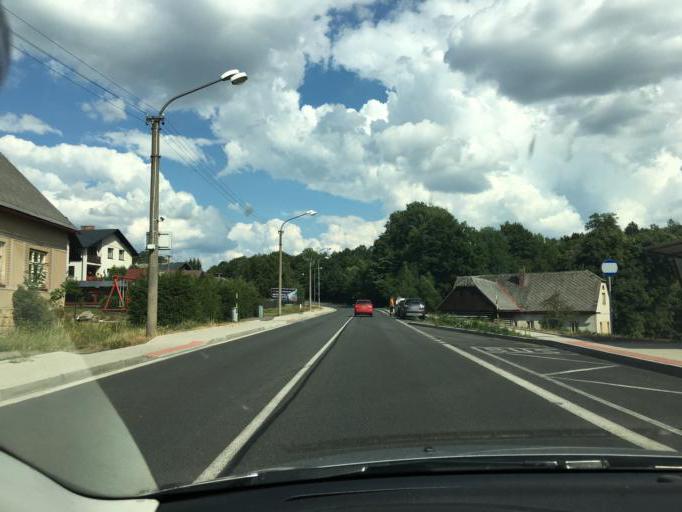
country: CZ
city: Horni Branna
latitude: 50.6211
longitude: 15.5606
